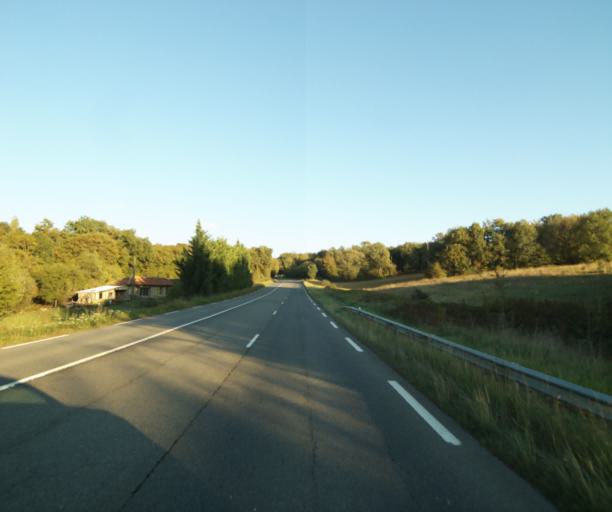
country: FR
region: Midi-Pyrenees
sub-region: Departement du Gers
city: Eauze
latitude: 43.7607
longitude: 0.1828
